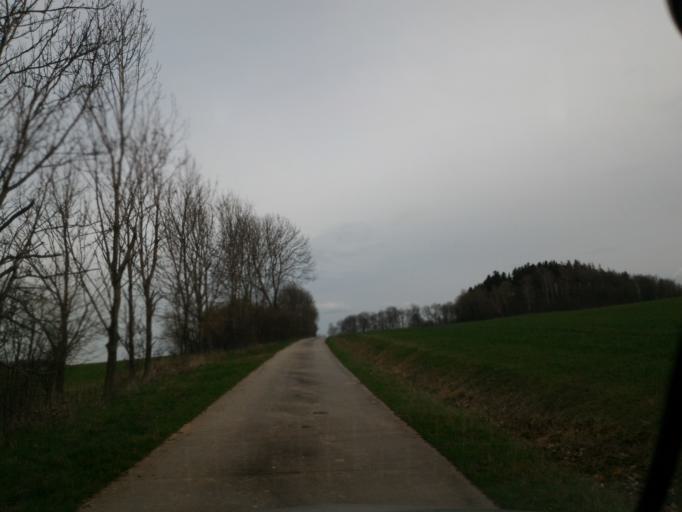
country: DE
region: Saxony
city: Grossschonau
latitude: 50.8796
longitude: 14.6964
